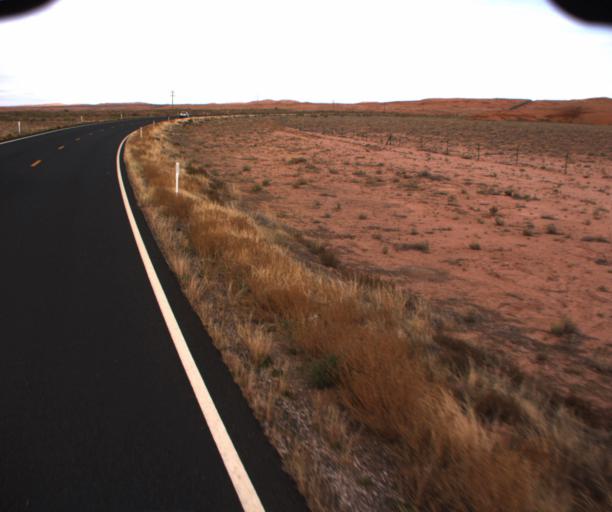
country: US
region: Arizona
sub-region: Apache County
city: Many Farms
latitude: 36.7720
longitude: -109.6610
